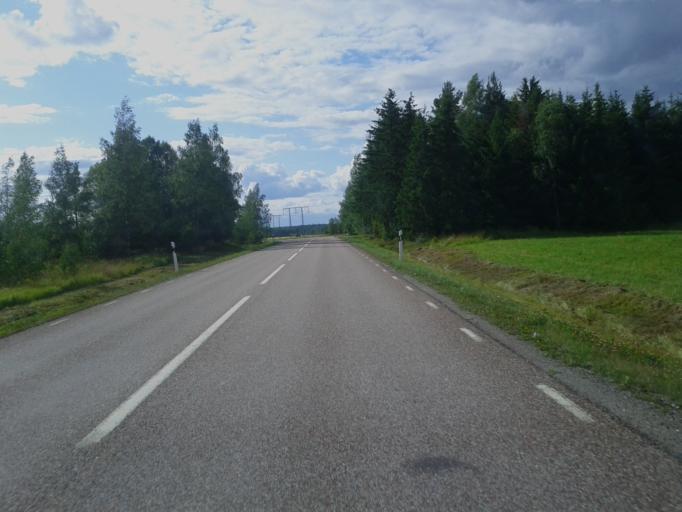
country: SE
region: Vaestmanland
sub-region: Sala Kommun
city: Sala
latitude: 59.9155
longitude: 16.5162
